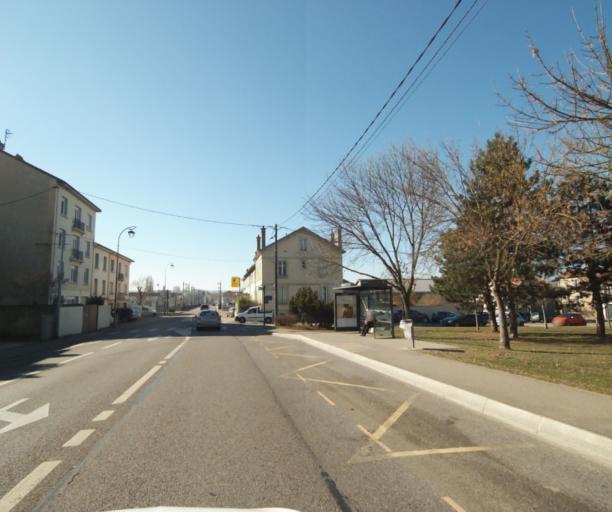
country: FR
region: Lorraine
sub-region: Departement de Meurthe-et-Moselle
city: Tomblaine
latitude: 48.6883
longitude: 6.2086
